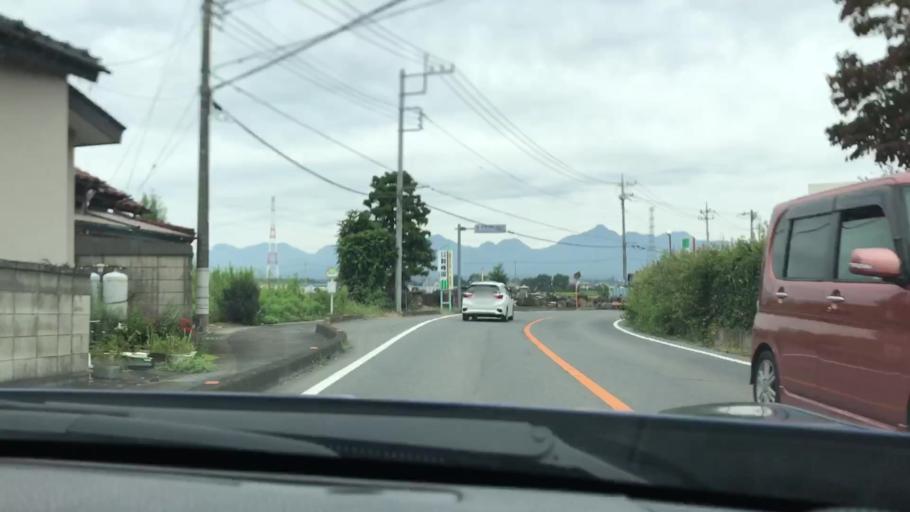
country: JP
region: Gunma
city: Kanekomachi
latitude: 36.3993
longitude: 138.9908
